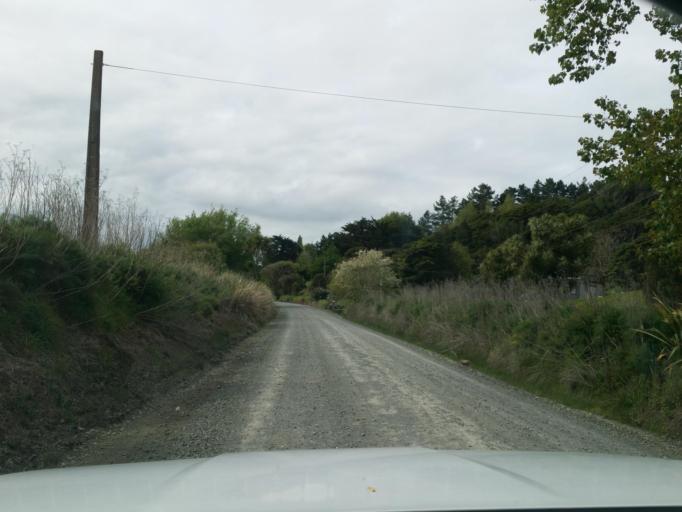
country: NZ
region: Northland
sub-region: Kaipara District
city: Dargaville
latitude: -35.9104
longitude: 173.9222
